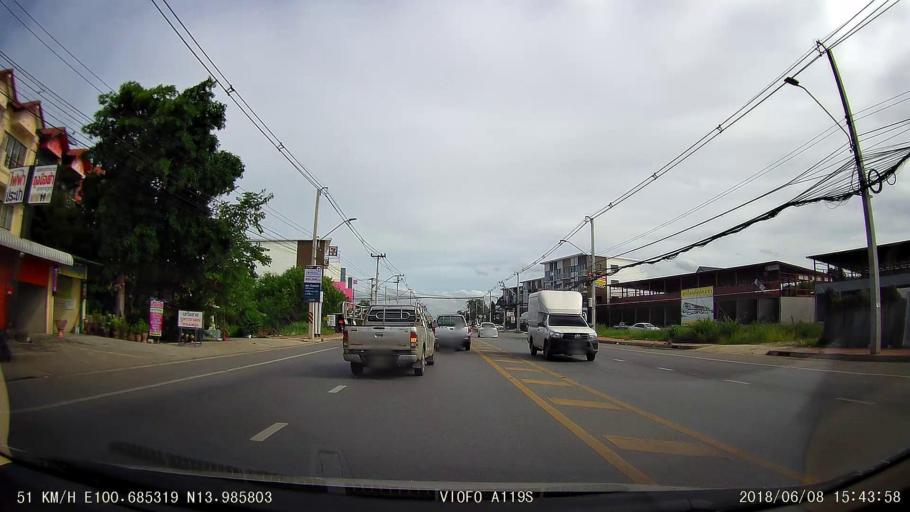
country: TH
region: Pathum Thani
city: Thanyaburi
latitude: 13.9857
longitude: 100.6853
